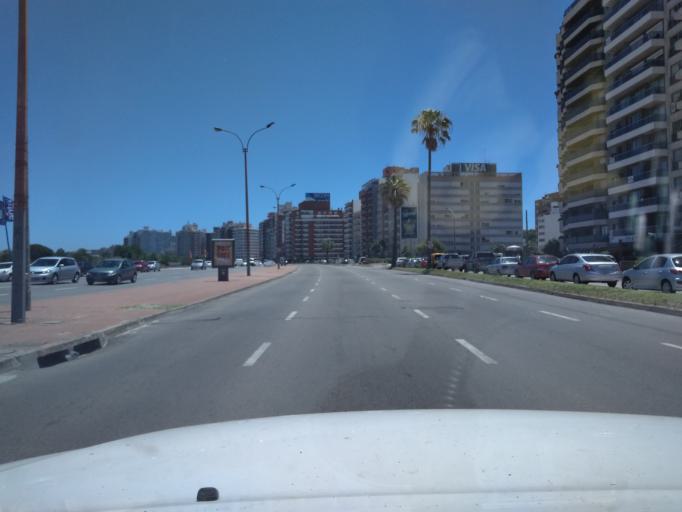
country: UY
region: Canelones
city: Paso de Carrasco
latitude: -34.8961
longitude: -56.1049
